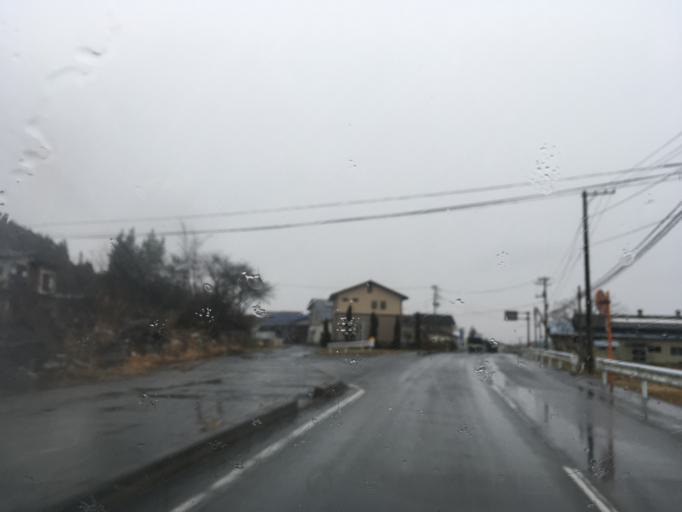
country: JP
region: Iwate
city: Ichinoseki
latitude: 38.8341
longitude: 140.9820
